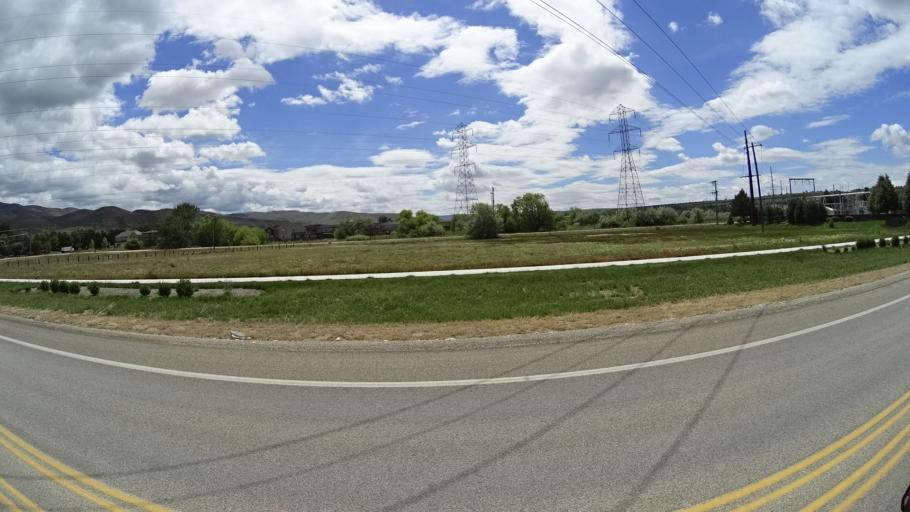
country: US
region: Idaho
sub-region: Ada County
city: Boise
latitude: 43.5706
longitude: -116.1269
